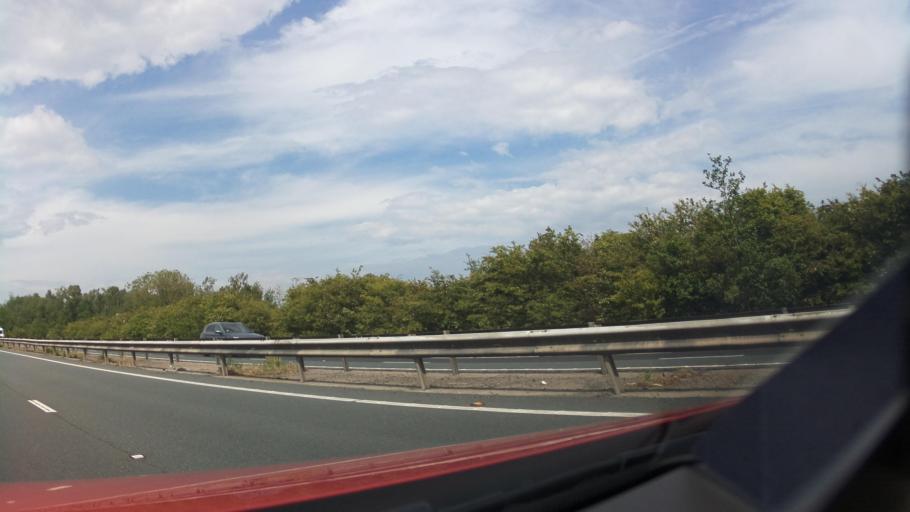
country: GB
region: England
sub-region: Northumberland
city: Felton
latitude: 55.3050
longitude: -1.7262
